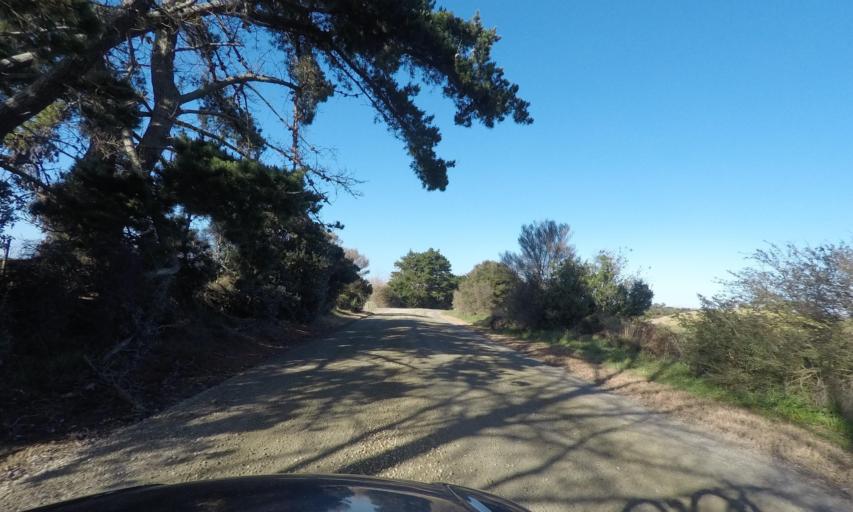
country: NZ
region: Auckland
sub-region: Auckland
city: Wellsford
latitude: -36.1492
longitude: 174.6066
